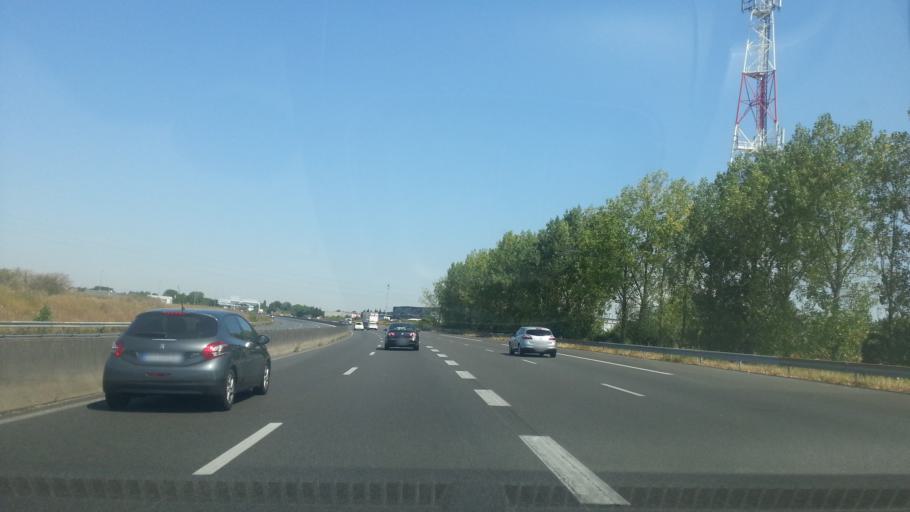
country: FR
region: Centre
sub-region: Departement du Loiret
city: Saint-Jean-de-la-Ruelle
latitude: 47.9063
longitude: 1.8494
